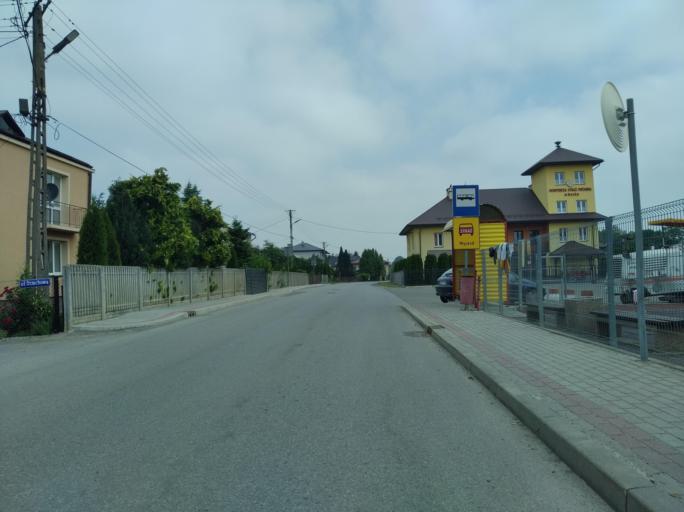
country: PL
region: Subcarpathian Voivodeship
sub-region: Powiat sanocki
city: Besko
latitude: 49.5919
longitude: 21.9582
